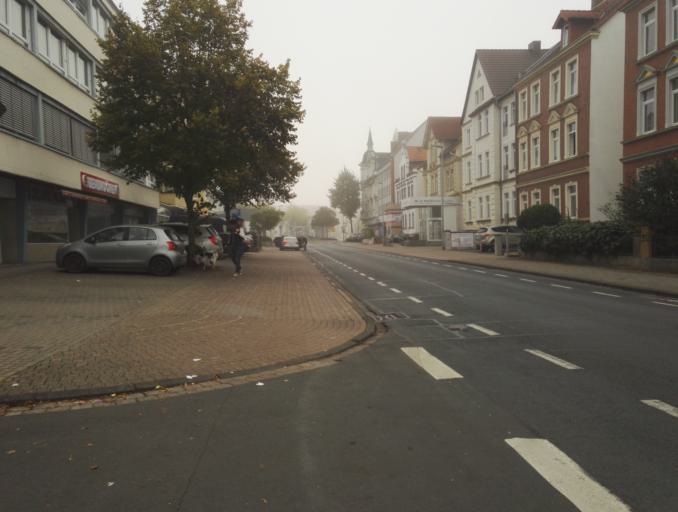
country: DE
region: Lower Saxony
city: Hameln
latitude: 52.1010
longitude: 9.3707
